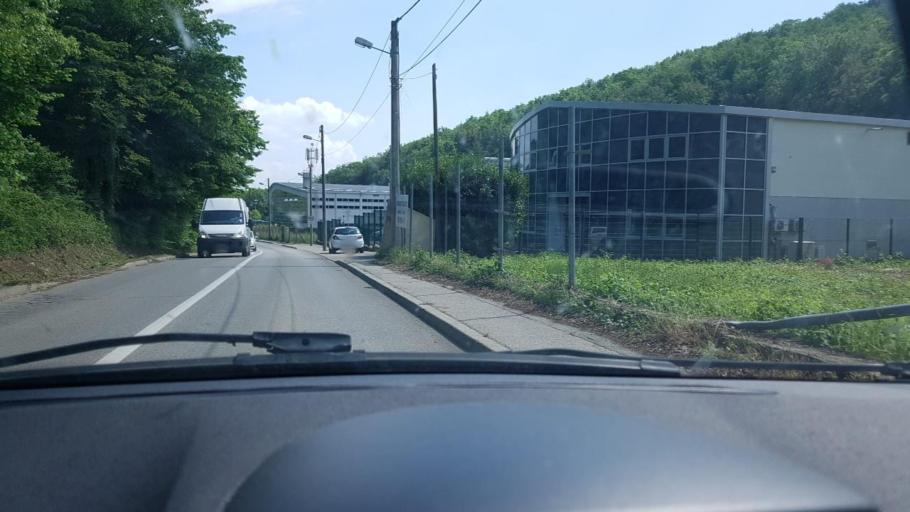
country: HR
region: Grad Zagreb
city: Dubrava
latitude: 45.8624
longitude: 16.0217
